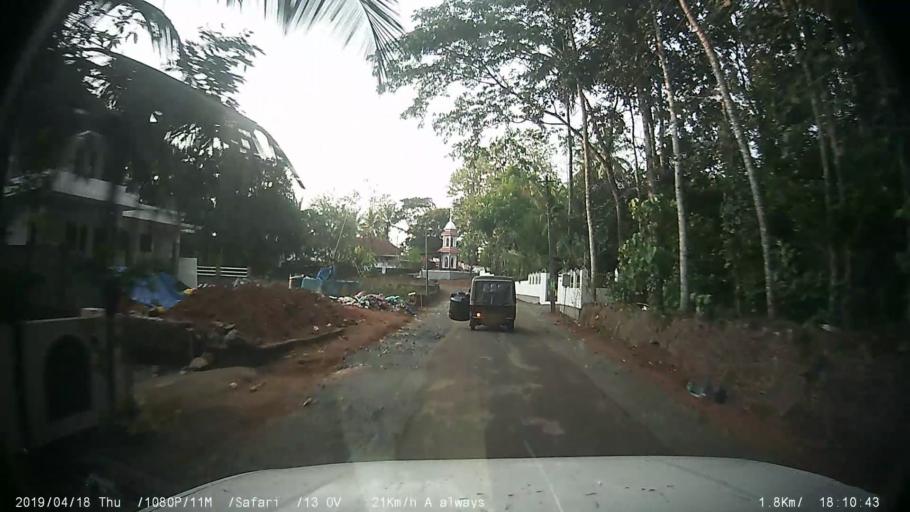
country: IN
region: Kerala
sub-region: Kottayam
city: Palackattumala
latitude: 9.7793
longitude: 76.5778
